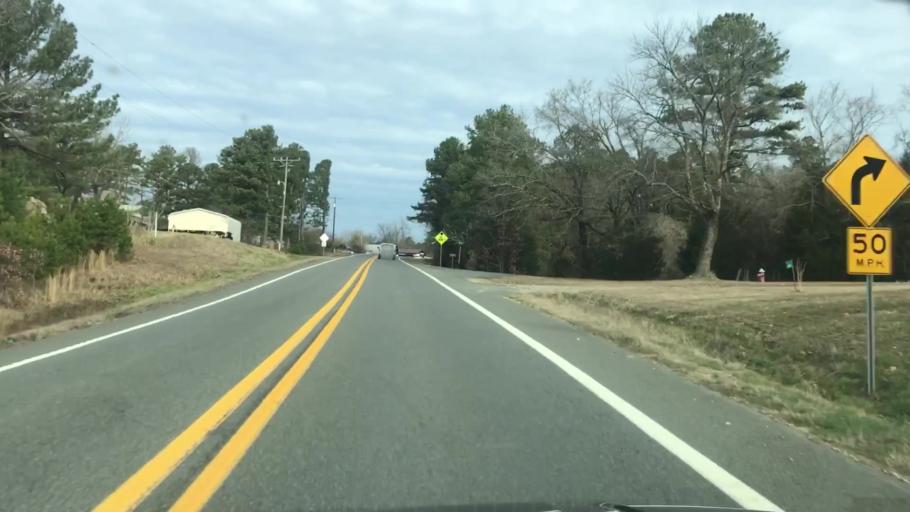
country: US
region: Arkansas
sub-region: Montgomery County
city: Mount Ida
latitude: 34.5831
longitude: -93.6626
